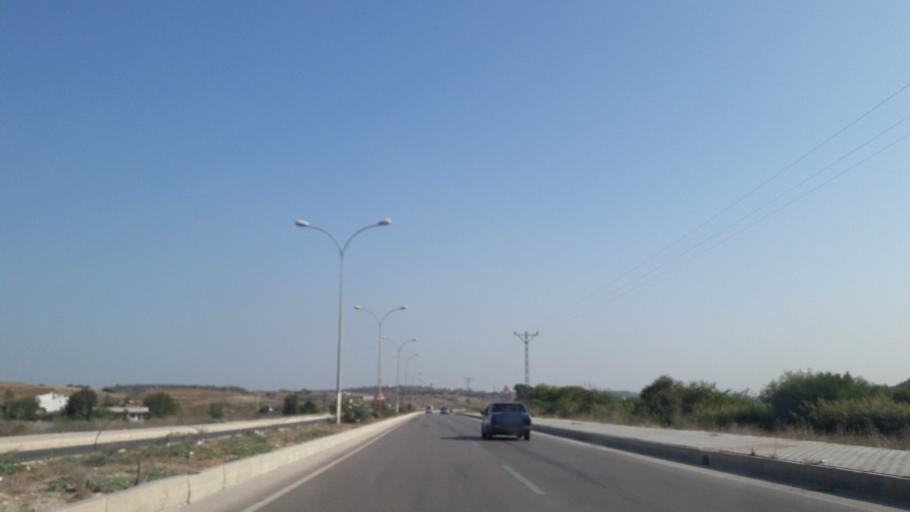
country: TR
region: Adana
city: Yuregir
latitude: 37.0585
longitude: 35.4434
